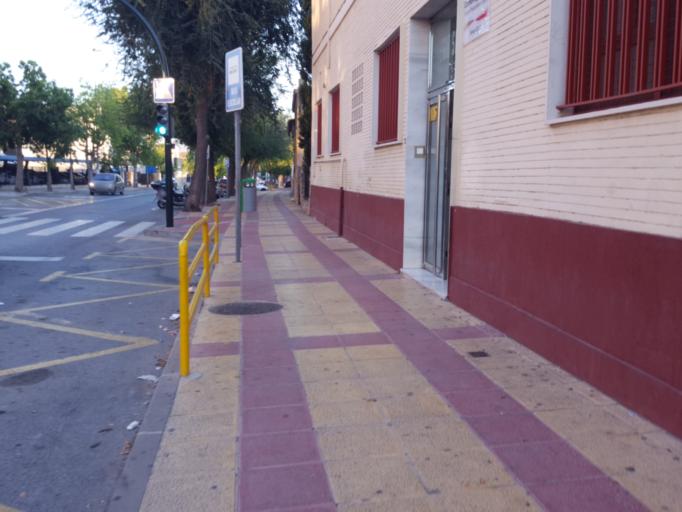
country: ES
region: Murcia
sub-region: Murcia
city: Murcia
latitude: 38.0054
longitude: -1.1488
